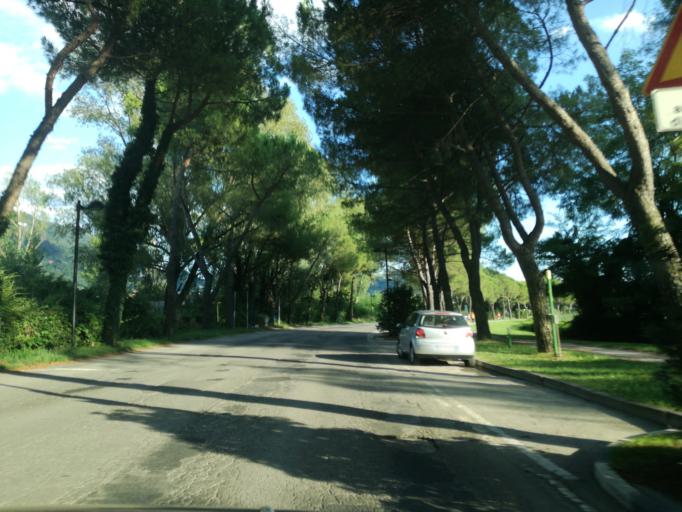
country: IT
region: Lombardy
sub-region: Provincia di Lecco
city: Calolziocorte
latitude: 45.7970
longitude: 9.4287
